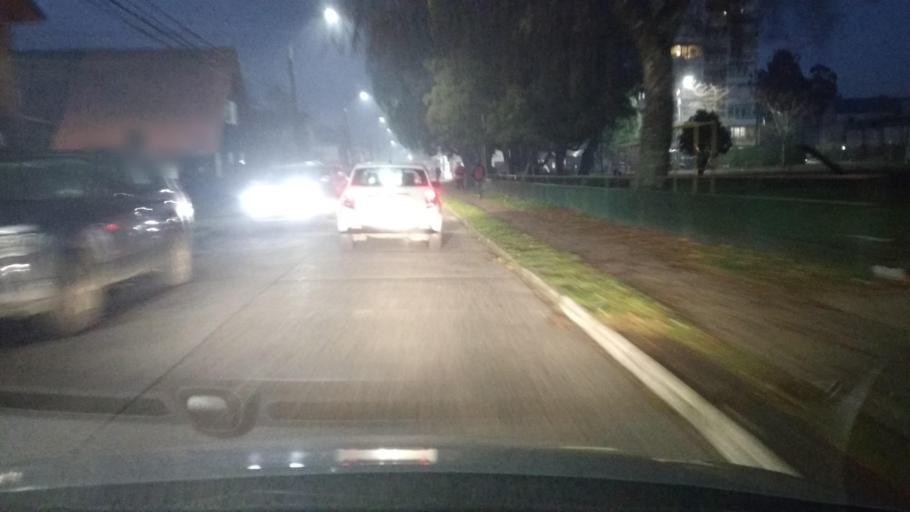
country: CL
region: Los Rios
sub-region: Provincia de Valdivia
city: Valdivia
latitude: -39.8147
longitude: -73.2577
